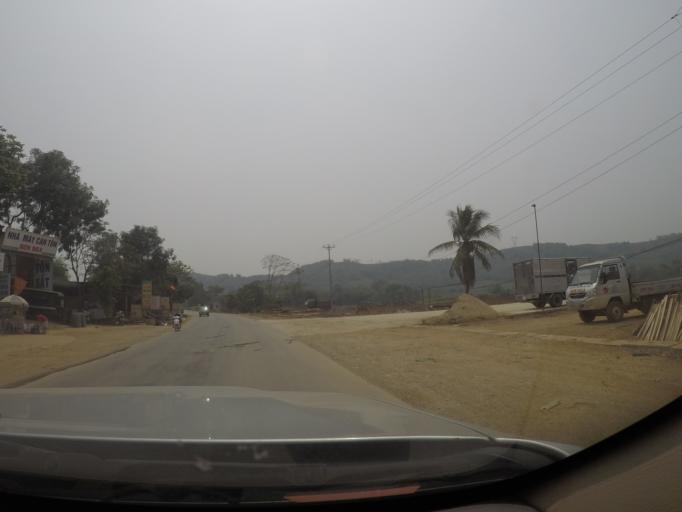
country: VN
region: Thanh Hoa
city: Thi Tran Thuong Xuan
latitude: 19.9647
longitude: 105.3977
